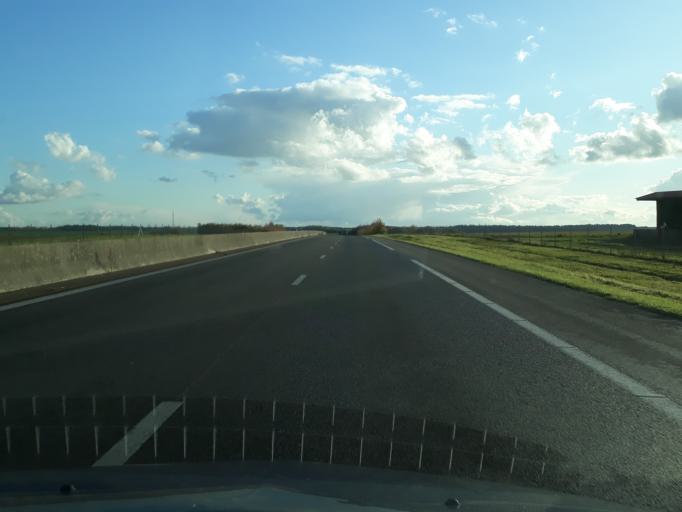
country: FR
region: Champagne-Ardenne
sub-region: Departement de la Marne
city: Fagnieres
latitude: 48.9271
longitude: 4.2835
